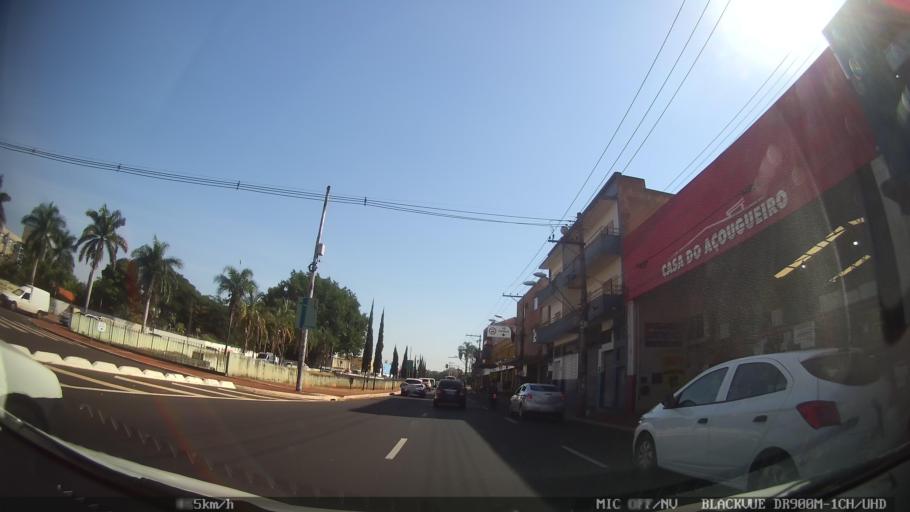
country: BR
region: Sao Paulo
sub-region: Ribeirao Preto
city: Ribeirao Preto
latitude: -21.1691
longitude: -47.8110
